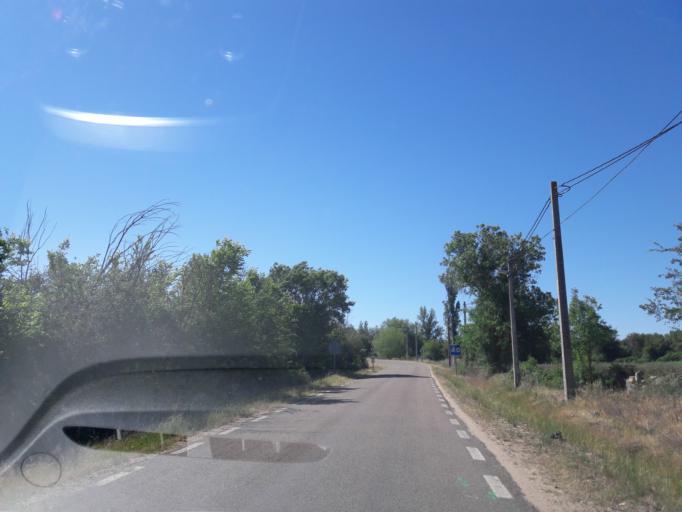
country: ES
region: Castille and Leon
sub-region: Provincia de Salamanca
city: Zarapicos
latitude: 41.0365
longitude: -5.8443
